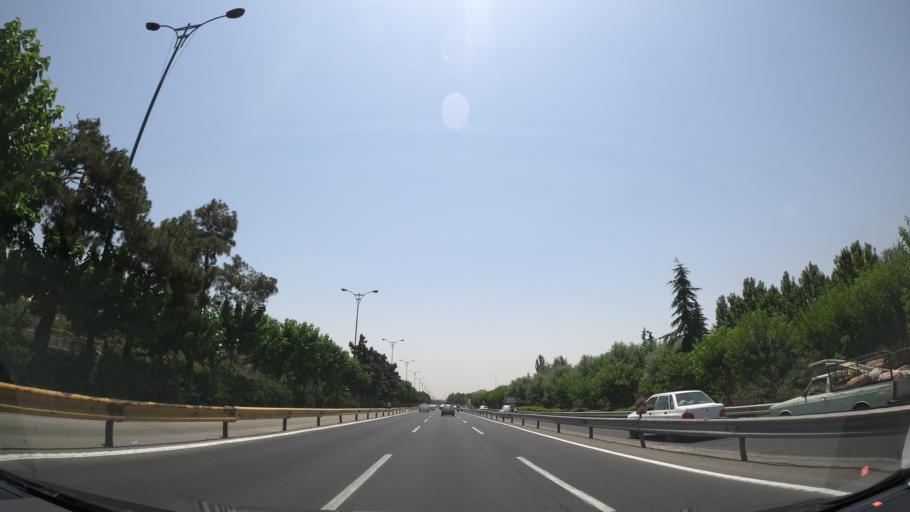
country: IR
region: Tehran
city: Tehran
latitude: 35.7361
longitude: 51.3833
